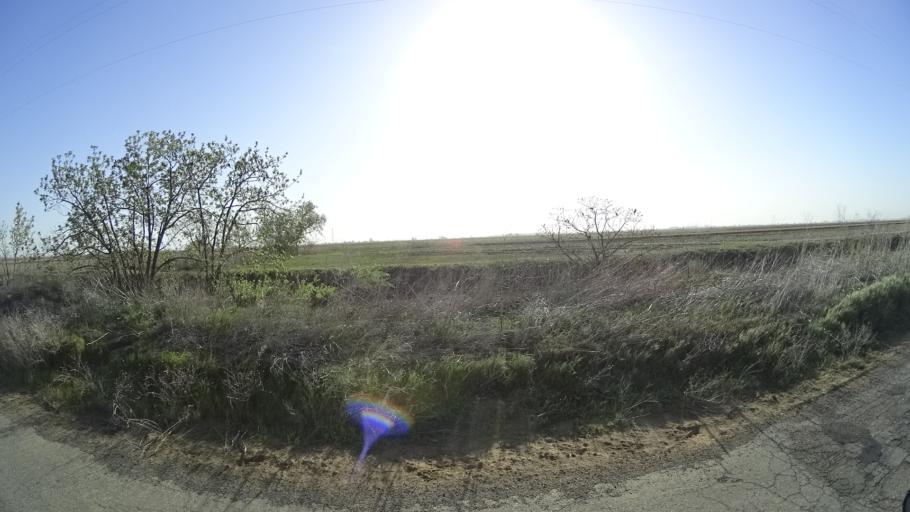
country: US
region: California
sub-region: Glenn County
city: Willows
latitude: 39.4032
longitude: -122.2300
